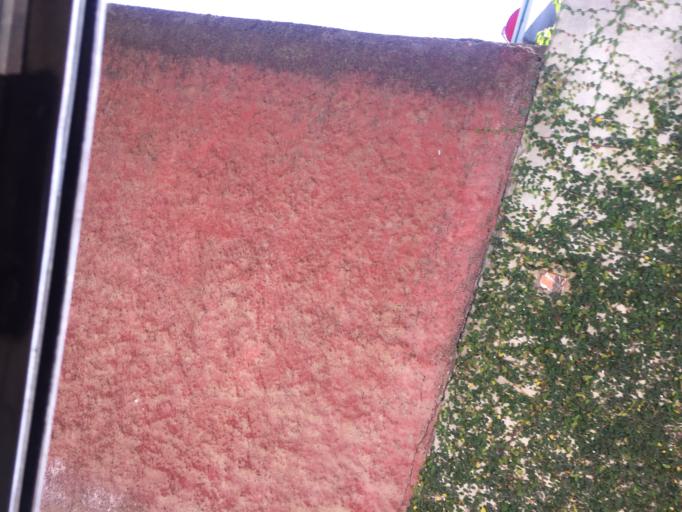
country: MX
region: Veracruz
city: El Castillo
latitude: 19.5320
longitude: -96.8856
